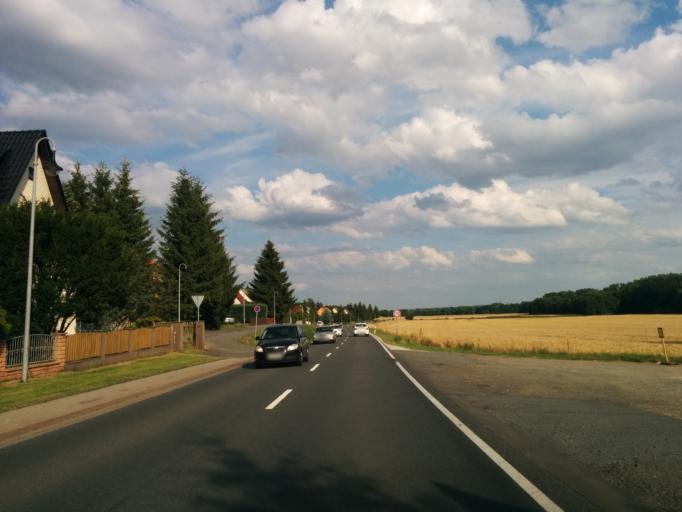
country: DE
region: Thuringia
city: Etzelsrode
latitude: 51.5209
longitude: 10.6681
